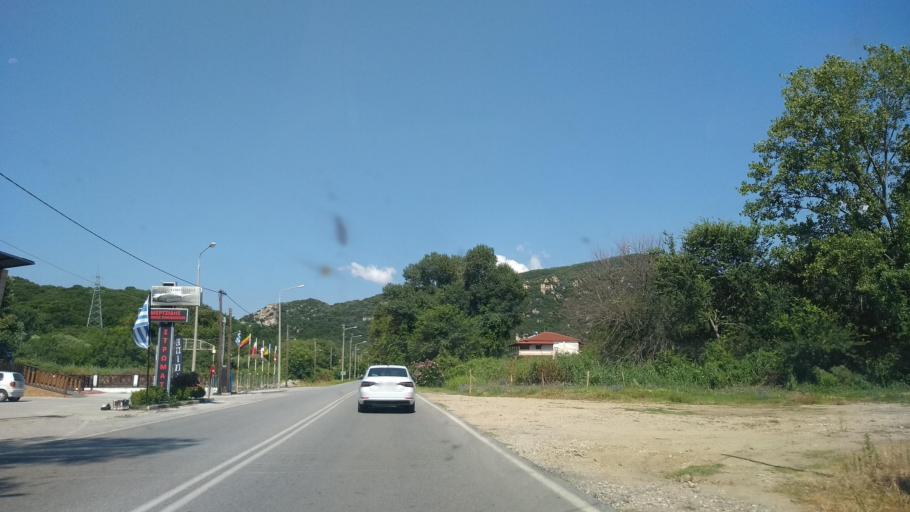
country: GR
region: Central Macedonia
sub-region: Nomos Thessalonikis
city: Stavros
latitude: 40.6695
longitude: 23.6698
